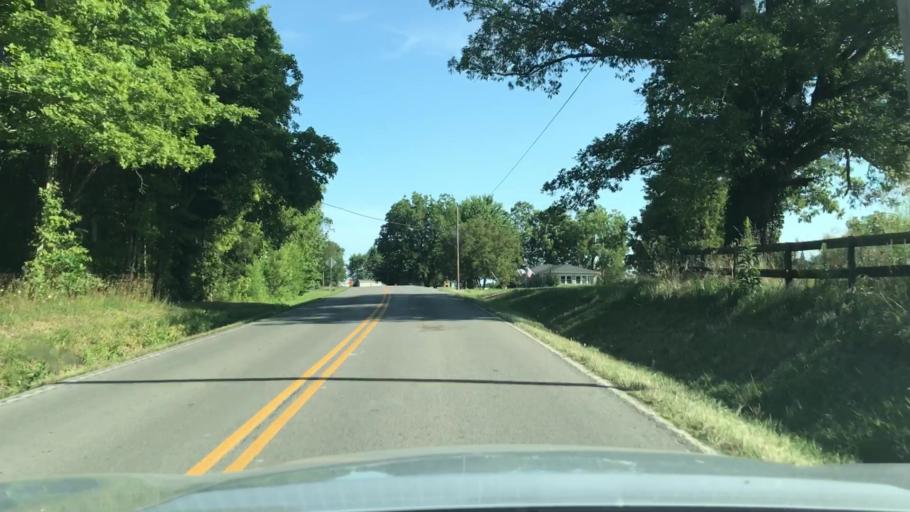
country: US
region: Kentucky
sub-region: Muhlenberg County
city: Greenville
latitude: 37.1605
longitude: -87.1423
